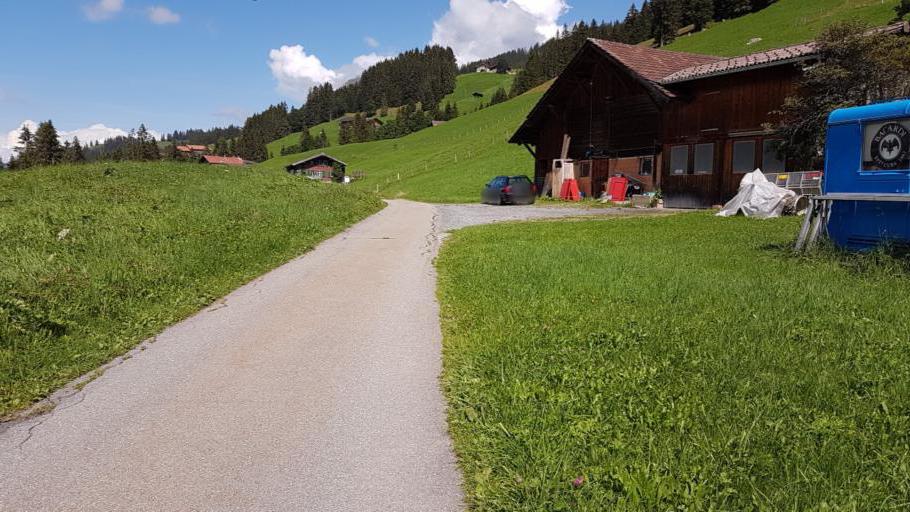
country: CH
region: Bern
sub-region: Frutigen-Niedersimmental District
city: Adelboden
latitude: 46.4971
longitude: 7.5837
